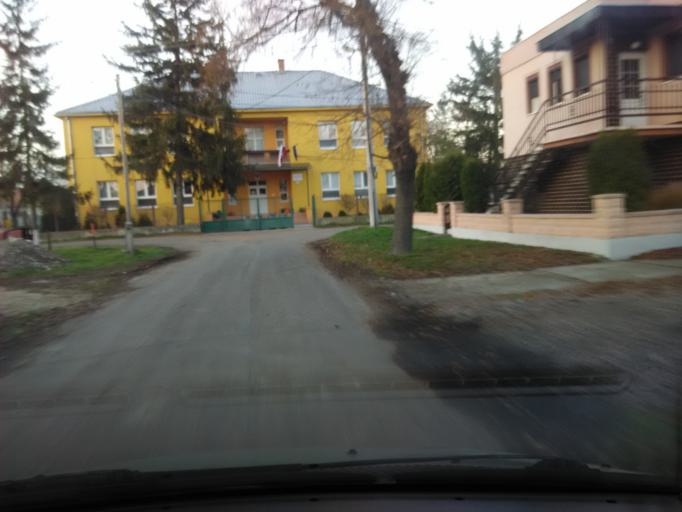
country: SK
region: Nitriansky
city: Tlmace
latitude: 48.2743
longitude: 18.5414
